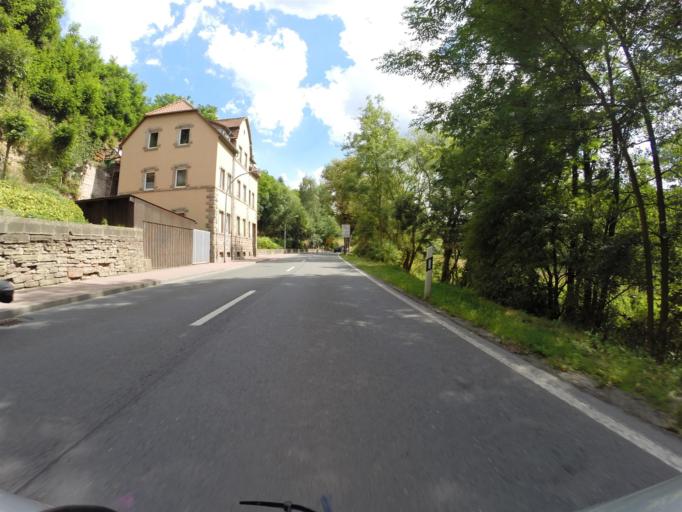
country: DE
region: Thuringia
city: Stadtroda
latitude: 50.8653
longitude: 11.7248
